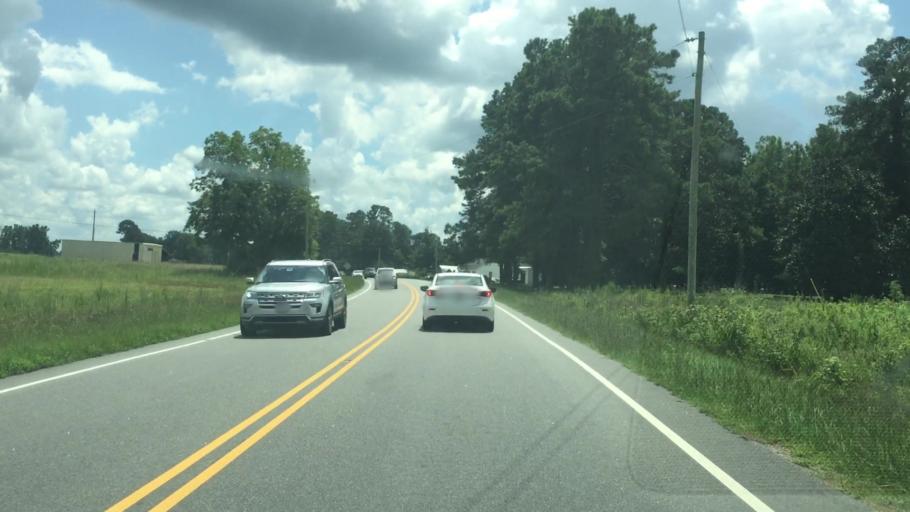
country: US
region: North Carolina
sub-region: Columbus County
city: Chadbourn
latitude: 34.2932
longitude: -78.8262
